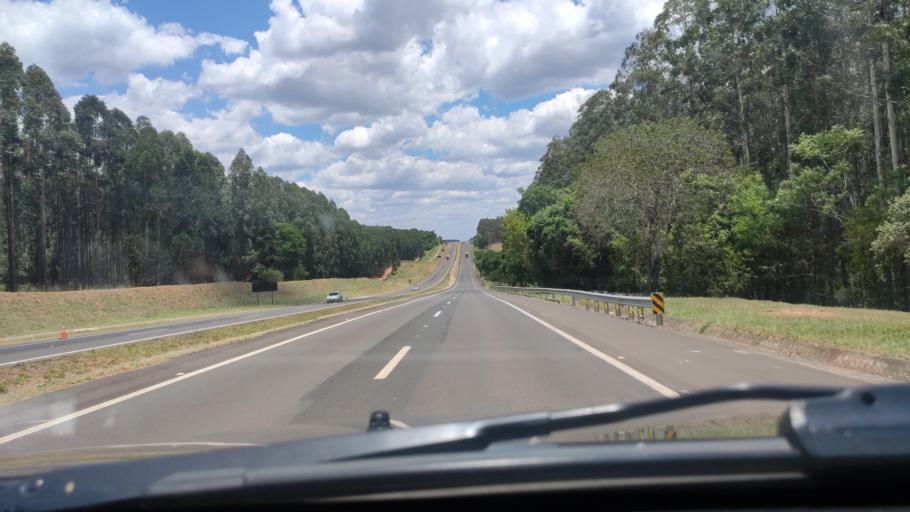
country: BR
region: Sao Paulo
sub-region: Duartina
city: Duartina
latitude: -22.4911
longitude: -49.2516
